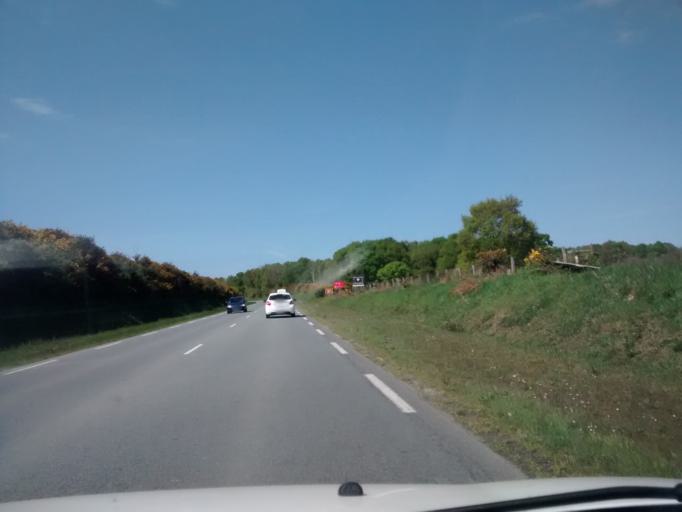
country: FR
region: Brittany
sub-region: Departement d'Ille-et-Vilaine
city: Pleurtuit
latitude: 48.5624
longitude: -2.0542
